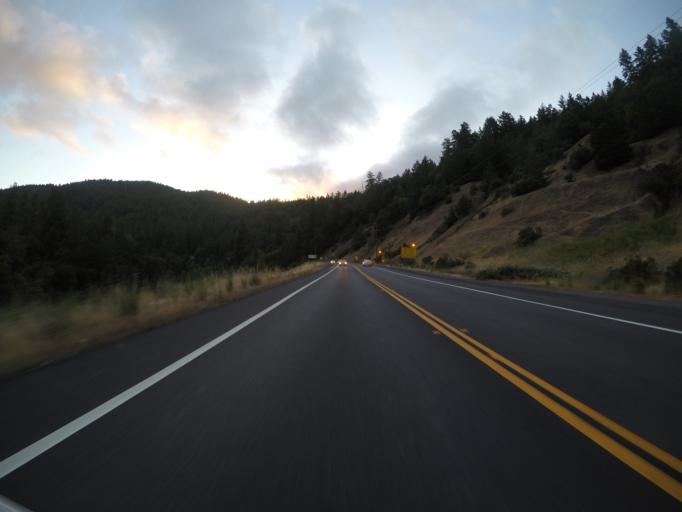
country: US
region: California
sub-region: Humboldt County
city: Redway
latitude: 40.0347
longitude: -123.7867
